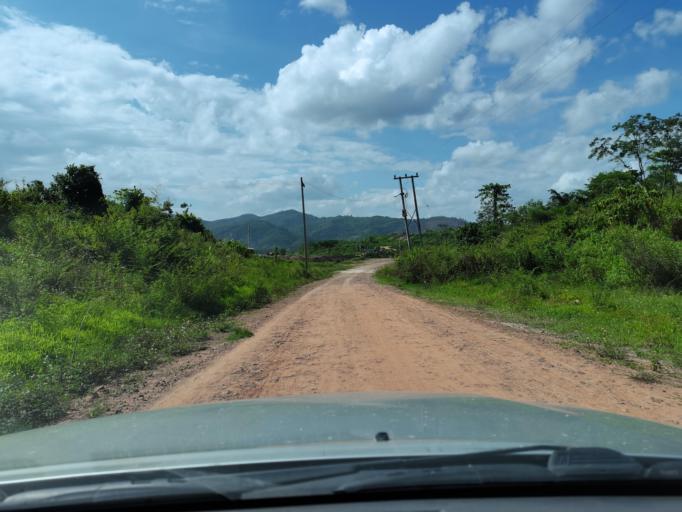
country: LA
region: Loungnamtha
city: Muang Nale
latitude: 20.5850
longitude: 101.0595
